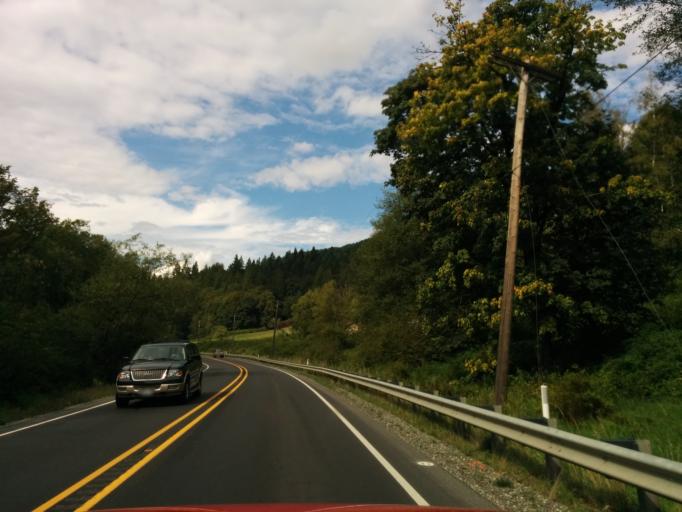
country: US
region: Washington
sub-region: King County
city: Duvall
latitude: 47.7695
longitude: -121.9556
